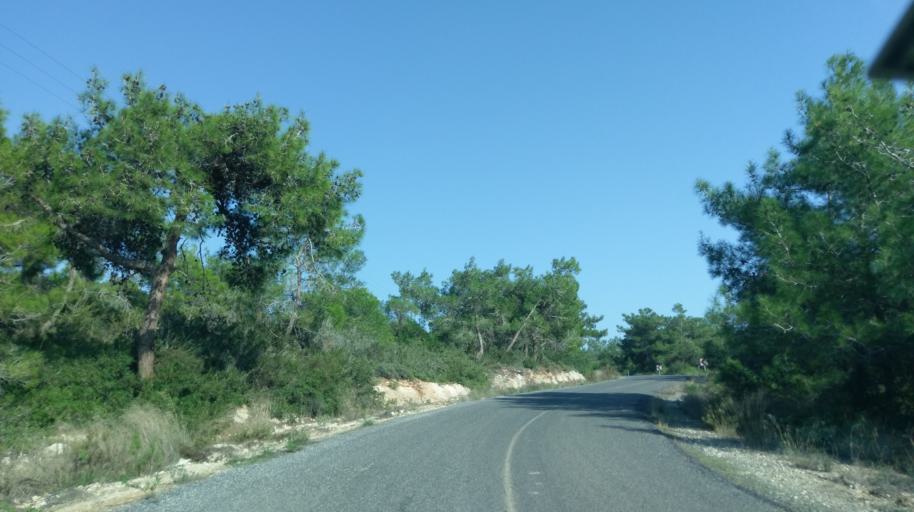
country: CY
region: Ammochostos
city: Leonarisso
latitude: 35.4886
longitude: 34.1886
